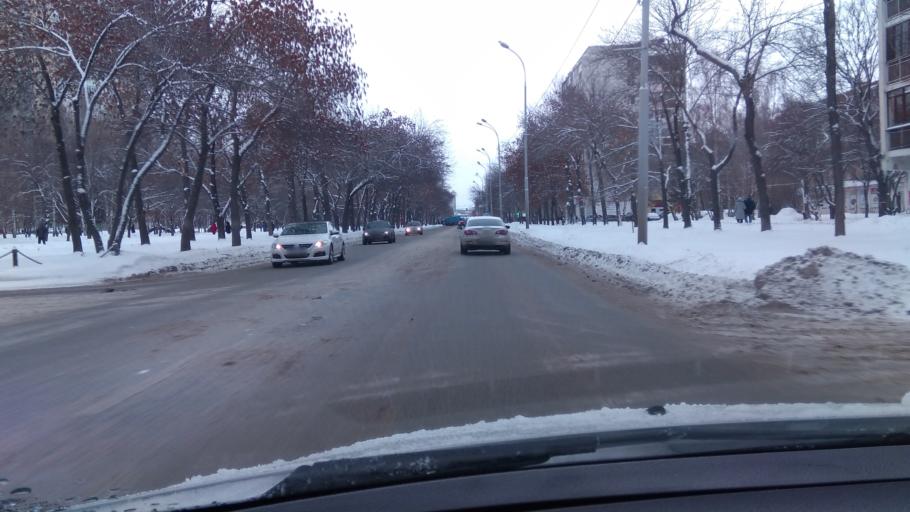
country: RU
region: Sverdlovsk
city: Sovkhoznyy
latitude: 56.8153
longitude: 60.5684
